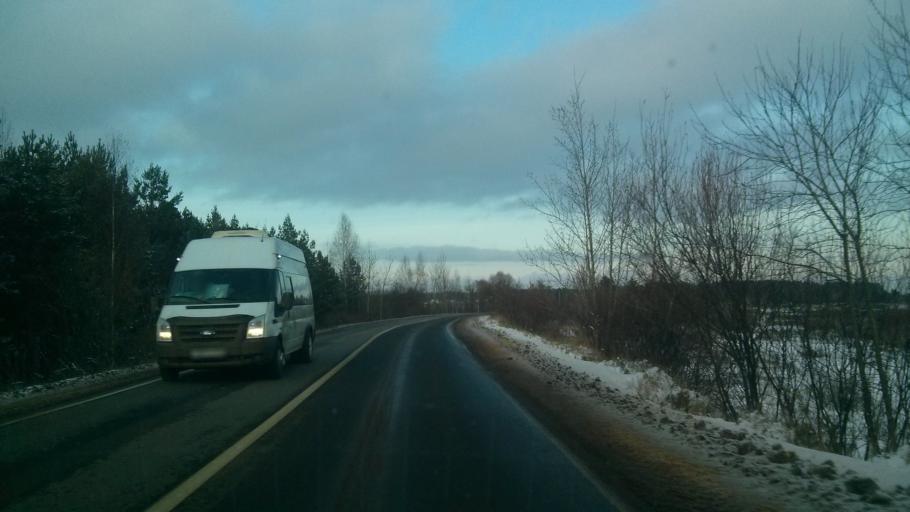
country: RU
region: Nizjnij Novgorod
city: Navashino
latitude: 55.5912
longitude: 42.1520
